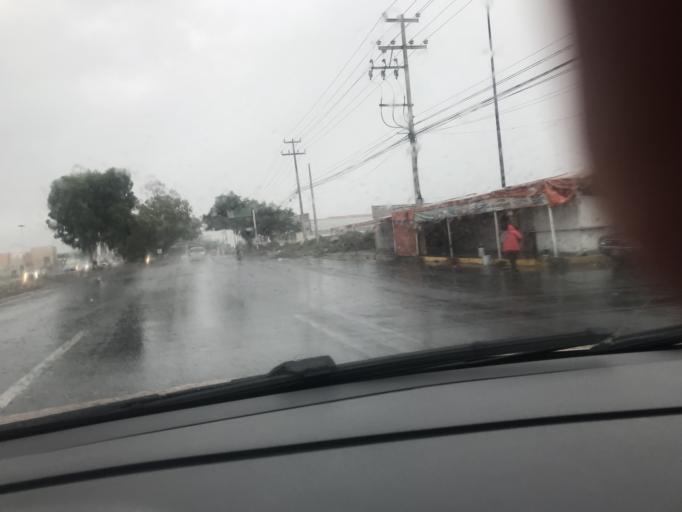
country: MX
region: Mexico
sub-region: Texcoco
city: Santa Martha
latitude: 19.4240
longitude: -98.9123
